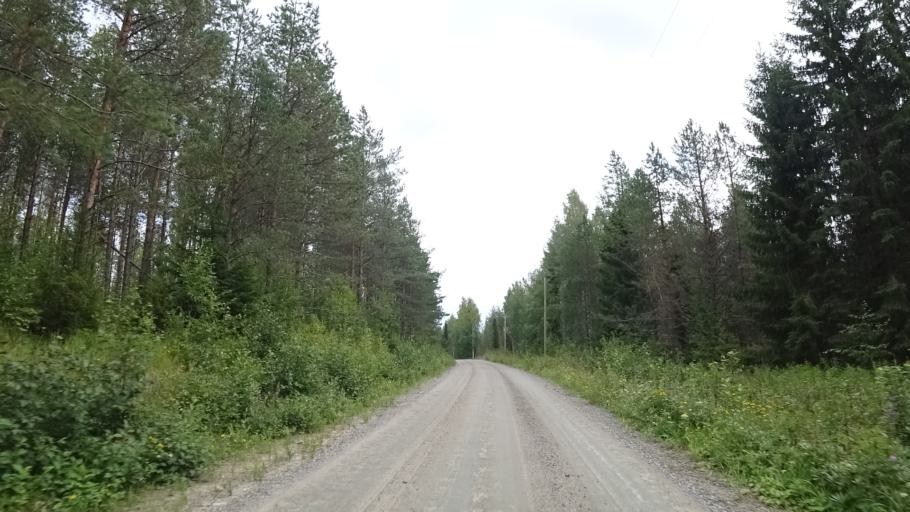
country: FI
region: North Karelia
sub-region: Joensuu
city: Ilomantsi
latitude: 62.9299
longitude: 31.3154
